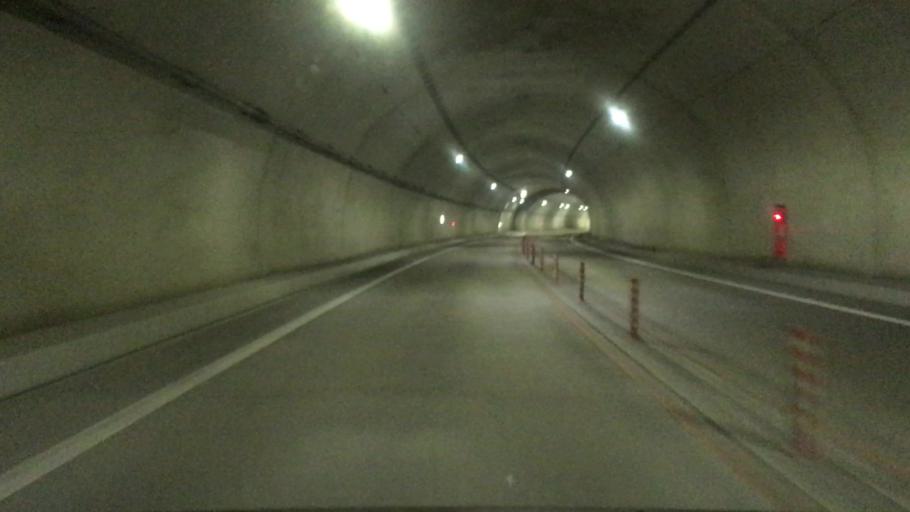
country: JP
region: Tottori
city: Tottori
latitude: 35.6258
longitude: 134.5194
